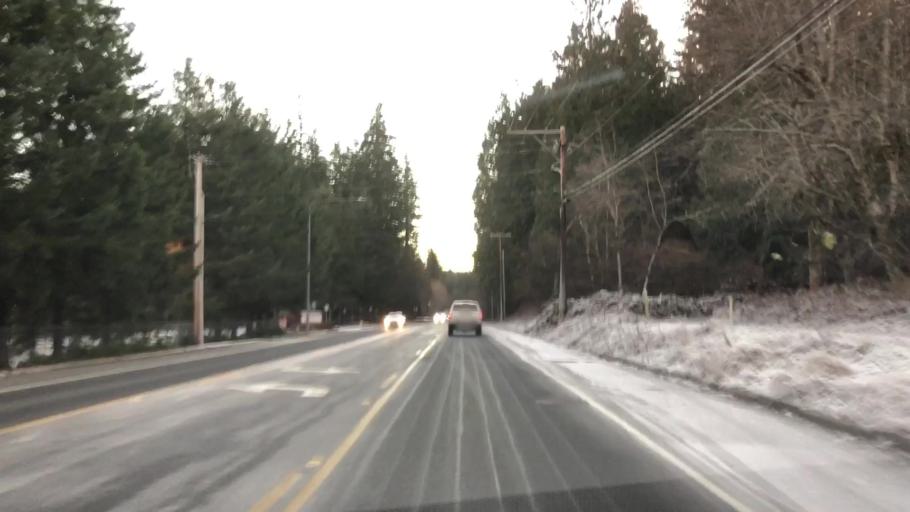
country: US
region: Washington
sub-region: King County
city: Union Hill-Novelty Hill
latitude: 47.7187
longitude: -122.0418
